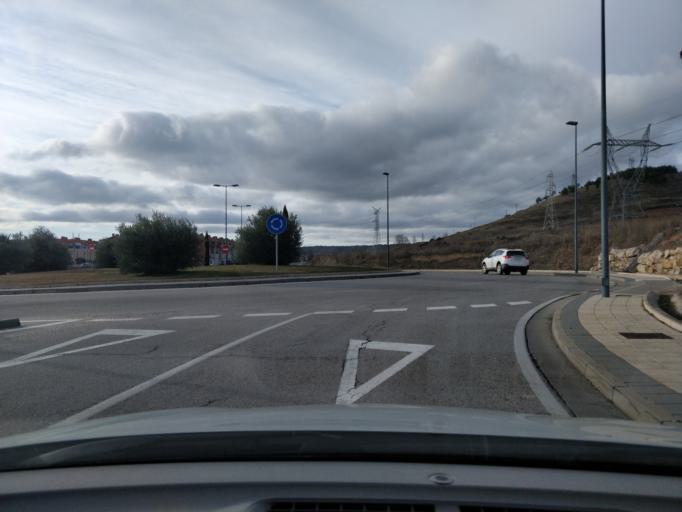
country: ES
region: Castille and Leon
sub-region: Provincia de Burgos
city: Villalbilla de Burgos
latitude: 42.3517
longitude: -3.7400
